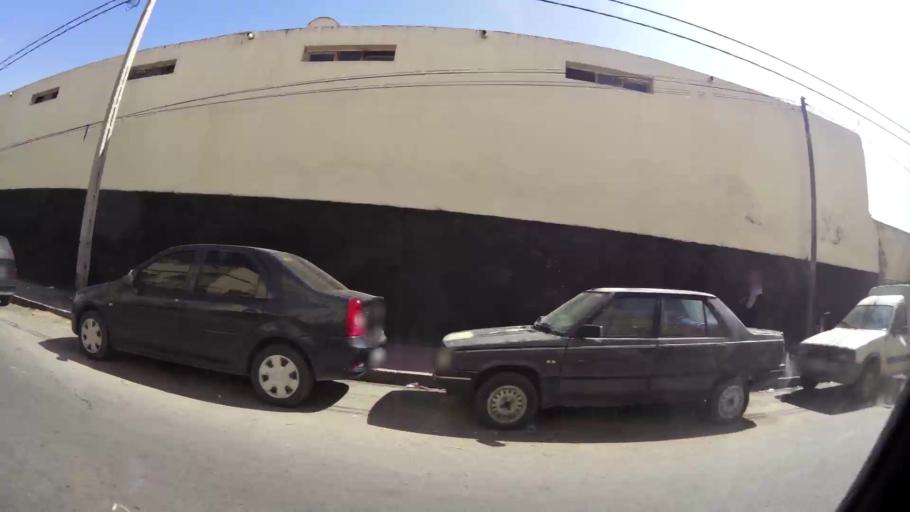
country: MA
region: Souss-Massa-Draa
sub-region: Inezgane-Ait Mellou
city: Inezgane
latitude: 30.3538
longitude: -9.5354
